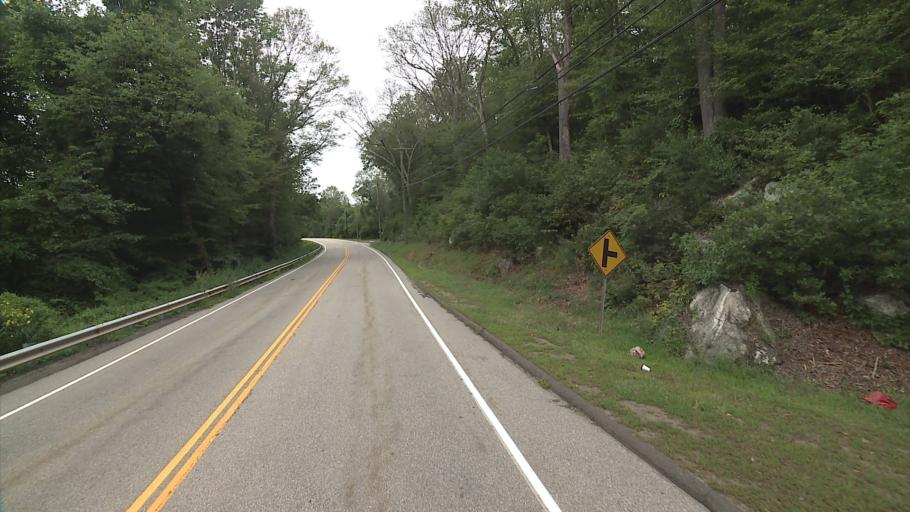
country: US
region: Connecticut
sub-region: Middlesex County
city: Essex Village
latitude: 41.4279
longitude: -72.3350
